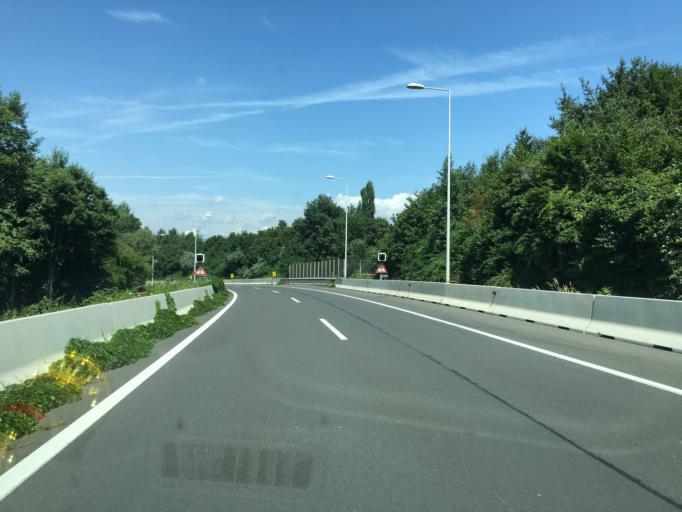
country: AT
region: Styria
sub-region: Graz Stadt
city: Wetzelsdorf
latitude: 47.0306
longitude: 15.4142
